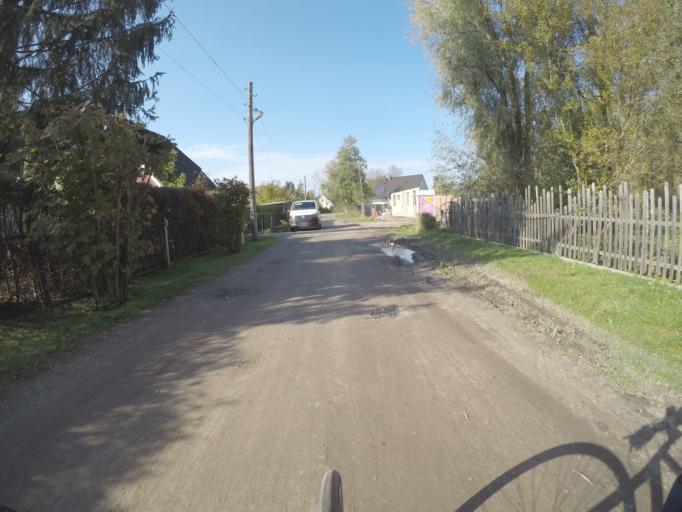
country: DE
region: Brandenburg
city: Oranienburg
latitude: 52.7236
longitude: 13.2472
